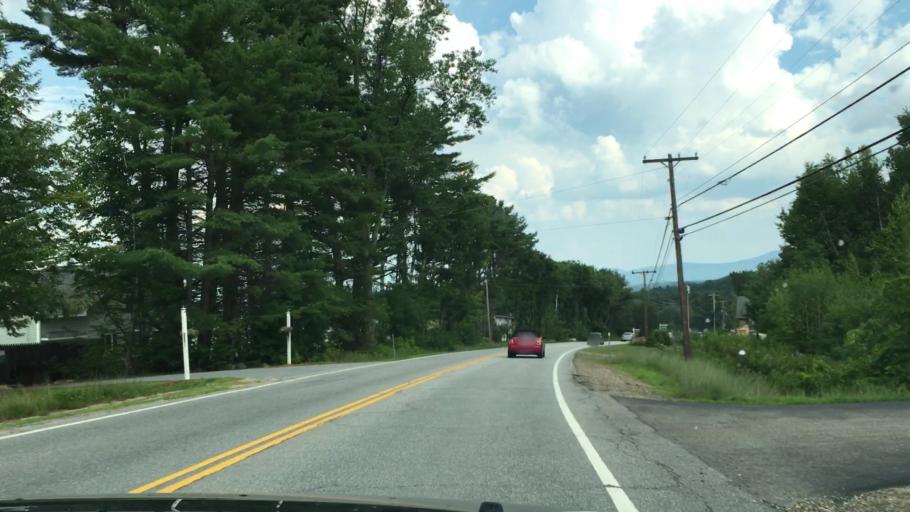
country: US
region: New Hampshire
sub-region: Belknap County
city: Meredith
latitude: 43.6364
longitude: -71.4910
